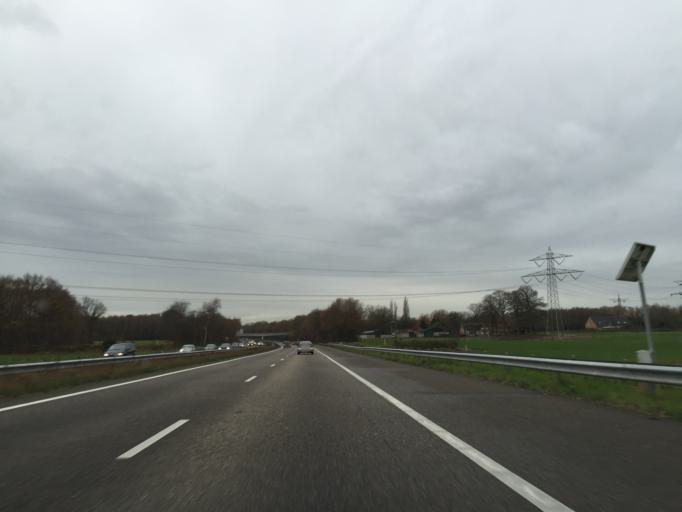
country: NL
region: North Brabant
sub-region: Gemeente Bergen op Zoom
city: Bergen op Zoom
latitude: 51.4721
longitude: 4.3127
